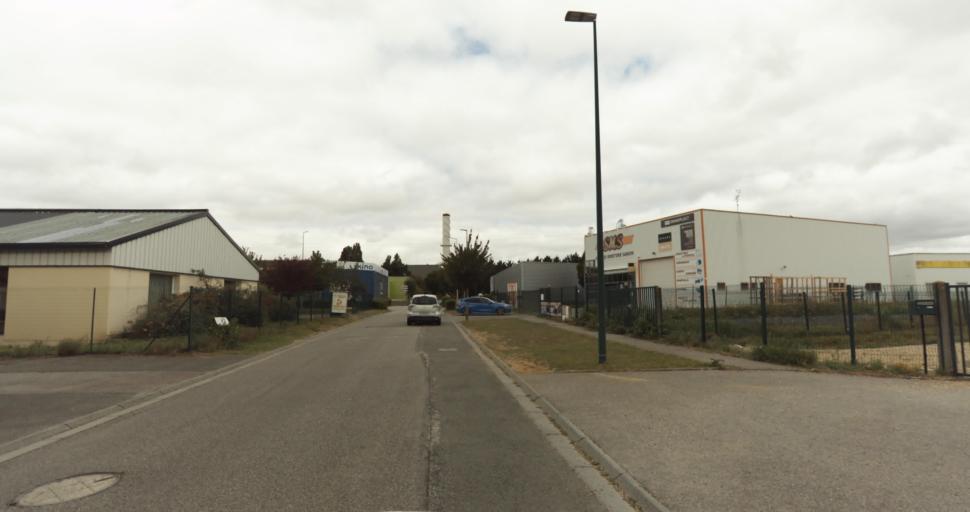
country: FR
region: Haute-Normandie
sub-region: Departement de l'Eure
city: Evreux
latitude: 49.0088
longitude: 1.1718
